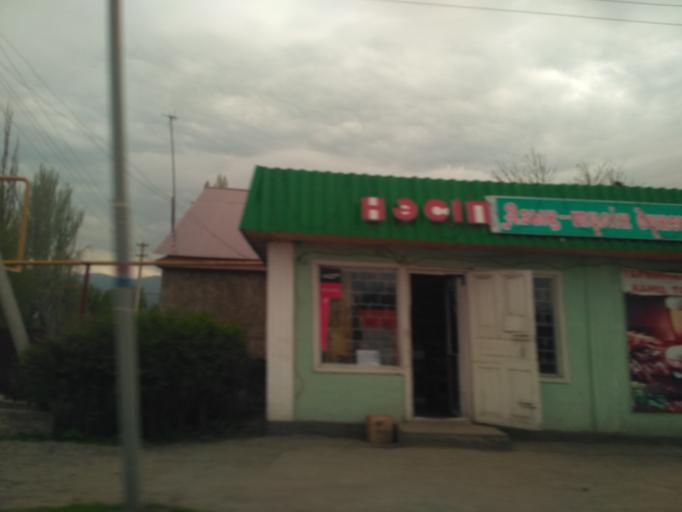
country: KZ
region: Almaty Oblysy
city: Burunday
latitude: 43.2108
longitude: 76.3255
